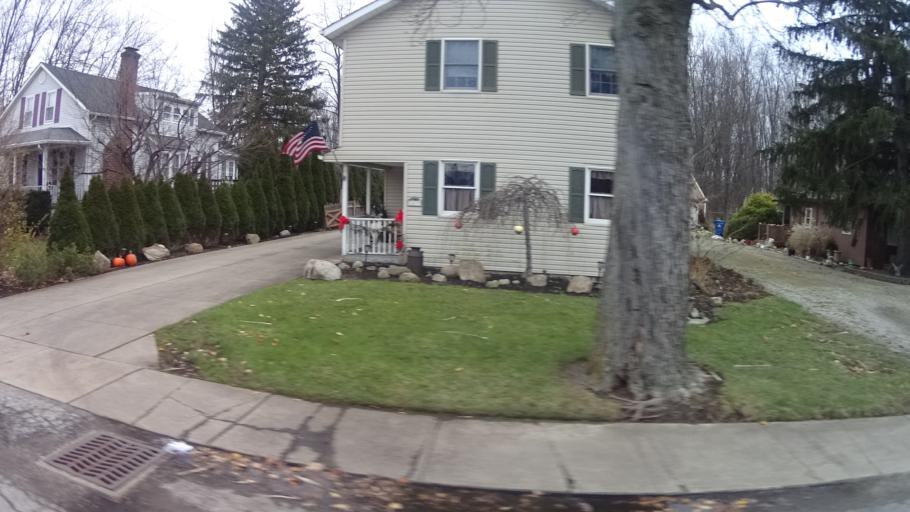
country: US
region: Ohio
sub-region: Lorain County
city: North Ridgeville
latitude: 41.3842
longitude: -82.0186
